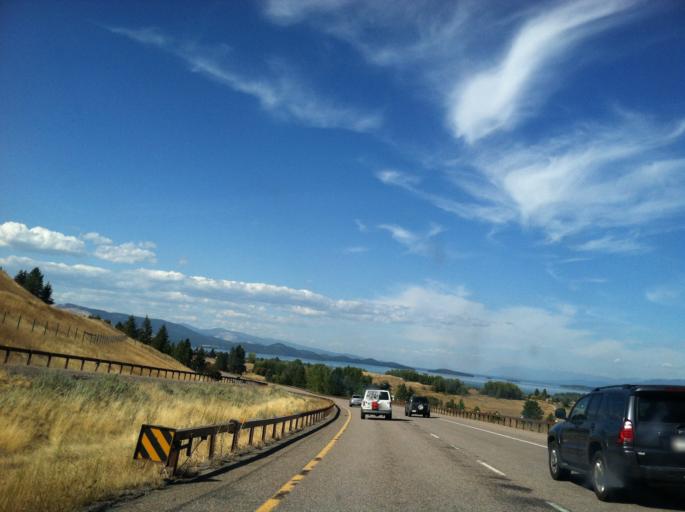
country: US
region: Montana
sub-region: Lake County
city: Polson
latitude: 47.6729
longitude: -114.1064
